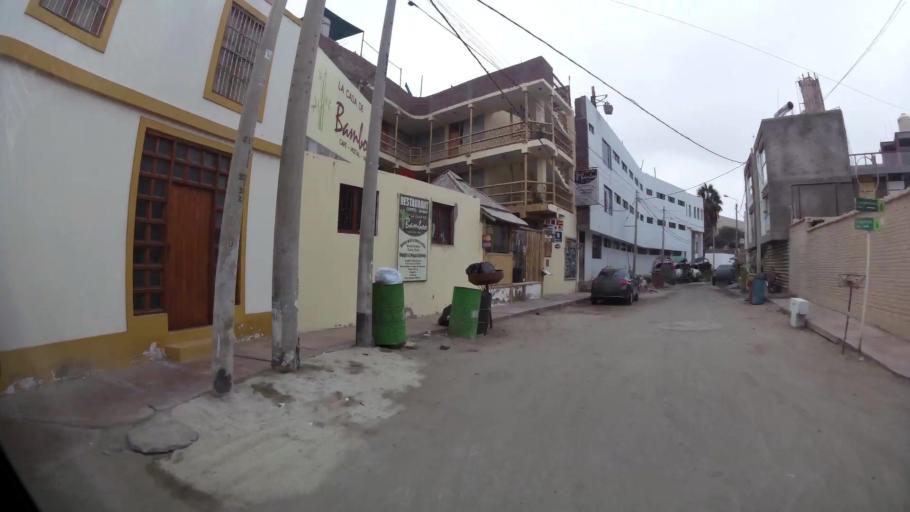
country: PE
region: Ica
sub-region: Provincia de Ica
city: Ica
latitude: -14.0868
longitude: -75.7649
